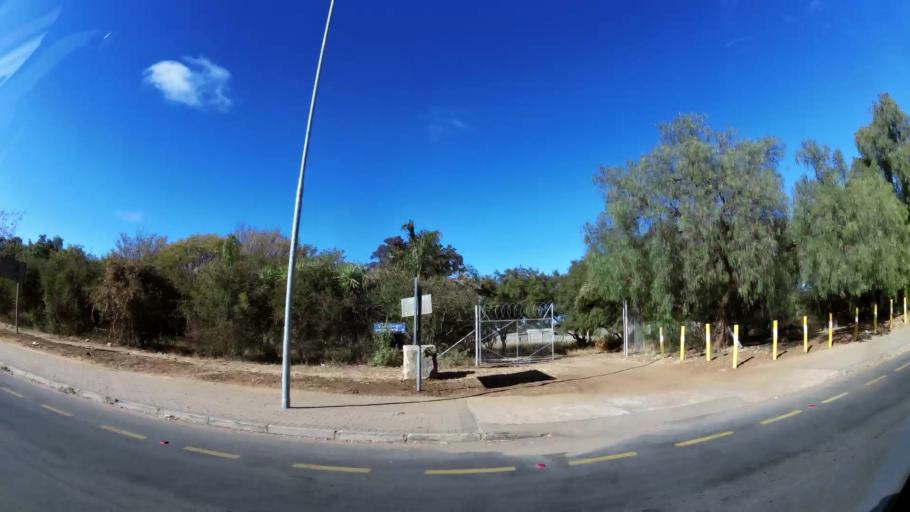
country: ZA
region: Limpopo
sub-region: Capricorn District Municipality
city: Polokwane
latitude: -23.9194
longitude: 29.4598
